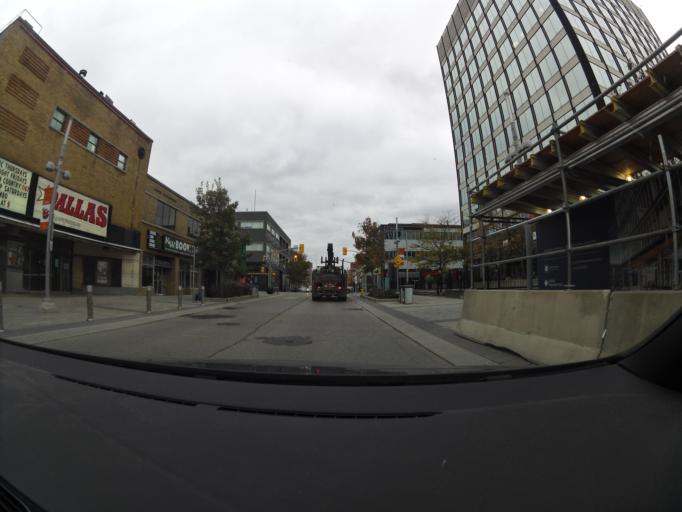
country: CA
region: Ontario
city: Waterloo
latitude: 43.4519
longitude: -80.4952
